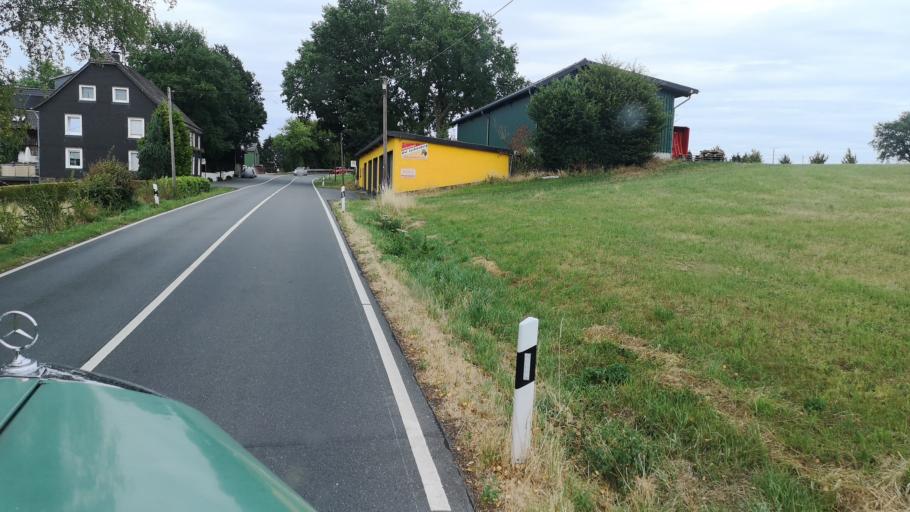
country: DE
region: North Rhine-Westphalia
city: Burscheid
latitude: 51.0802
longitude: 7.1565
